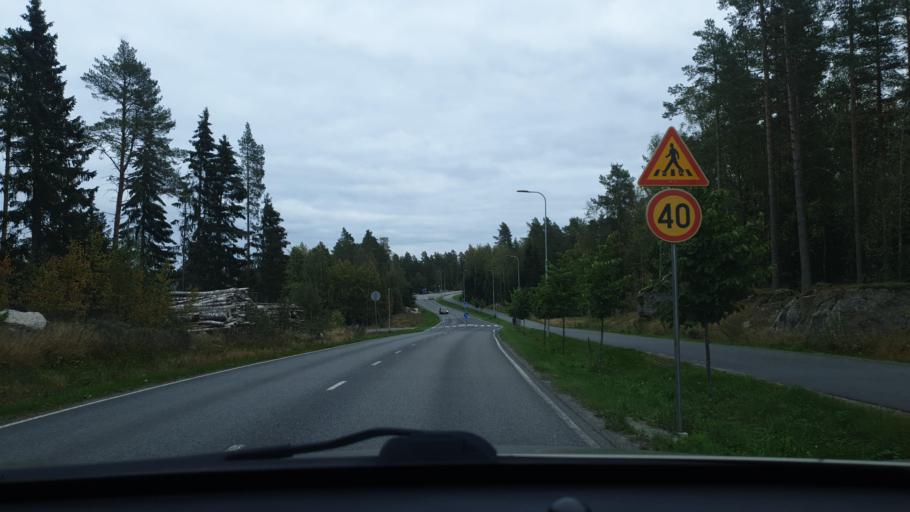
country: FI
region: Ostrobothnia
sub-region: Vaasa
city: Korsholm
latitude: 63.1203
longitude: 21.6515
